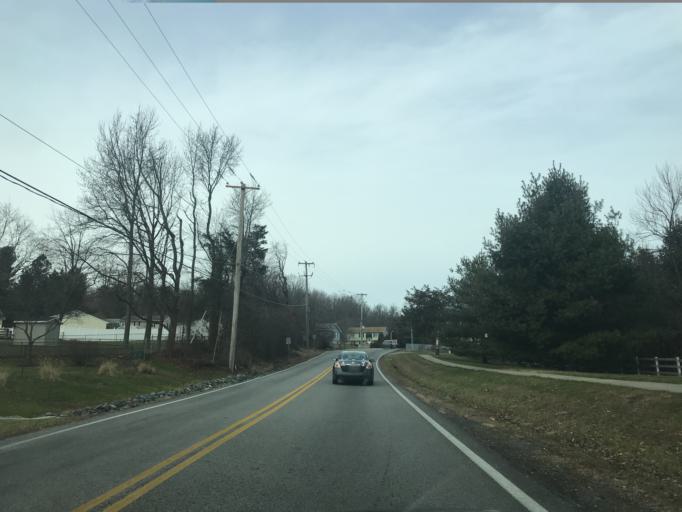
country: US
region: Maryland
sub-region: Cecil County
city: Elkton
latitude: 39.6099
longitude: -75.7915
